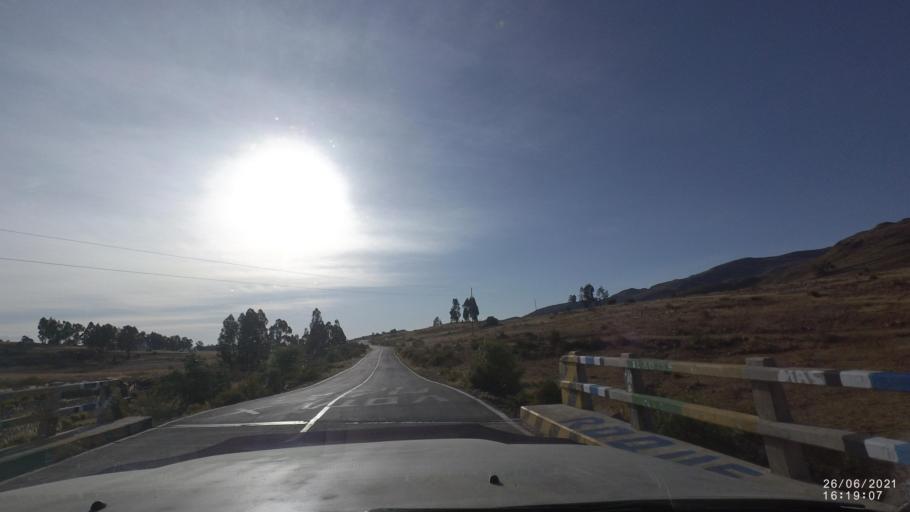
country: BO
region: Cochabamba
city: Arani
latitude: -17.7977
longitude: -65.8014
